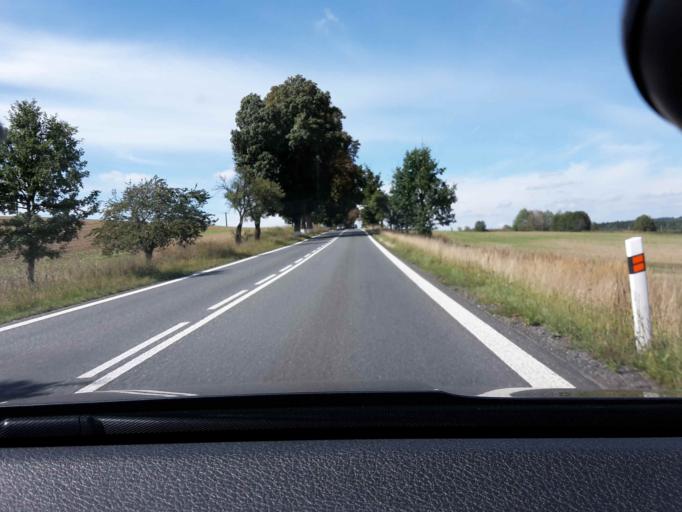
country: CZ
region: Jihocesky
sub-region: Okres Jindrichuv Hradec
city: Jindrichuv Hradec
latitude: 49.1566
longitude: 14.9729
